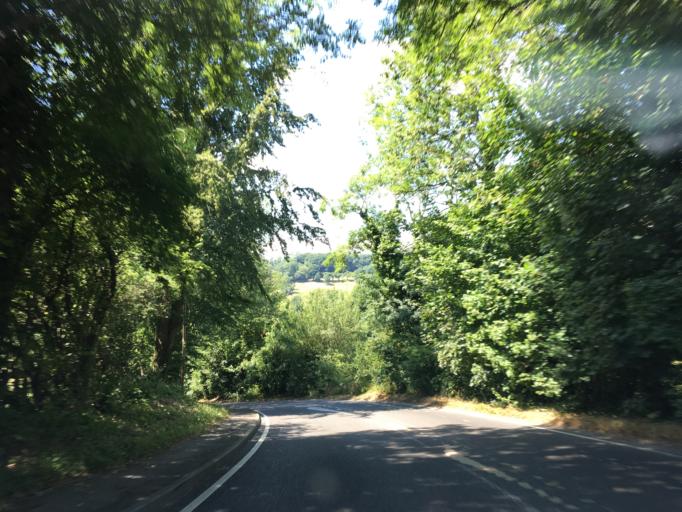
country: GB
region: England
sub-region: Gloucestershire
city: Chalford
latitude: 51.7348
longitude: -2.1695
